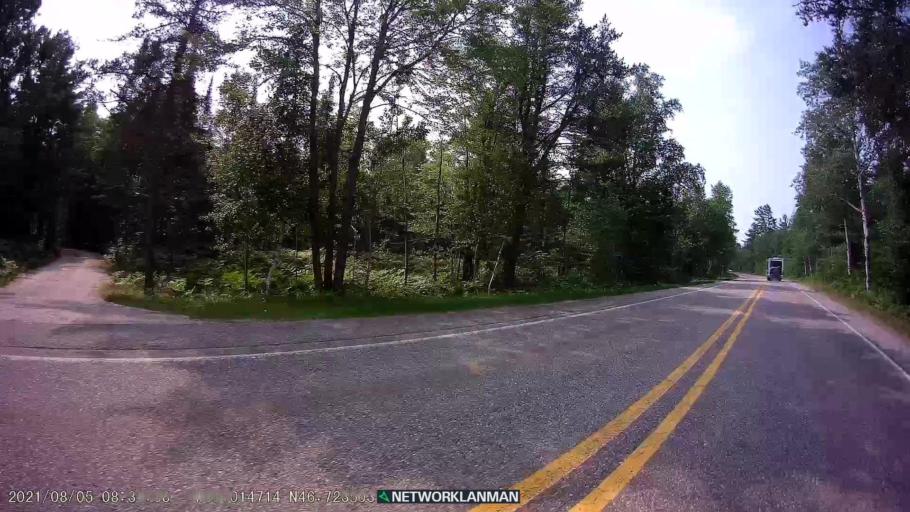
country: US
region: Michigan
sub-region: Luce County
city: Newberry
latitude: 46.7235
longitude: -85.0151
